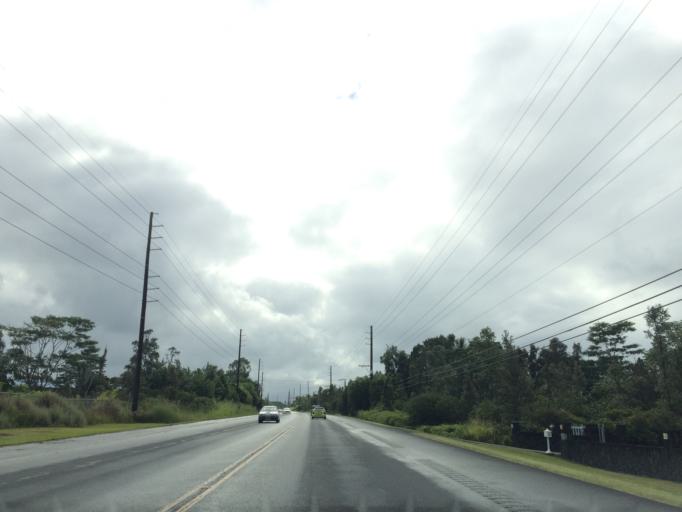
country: US
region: Hawaii
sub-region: Hawaii County
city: Ainaloa
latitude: 19.5493
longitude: -154.9813
